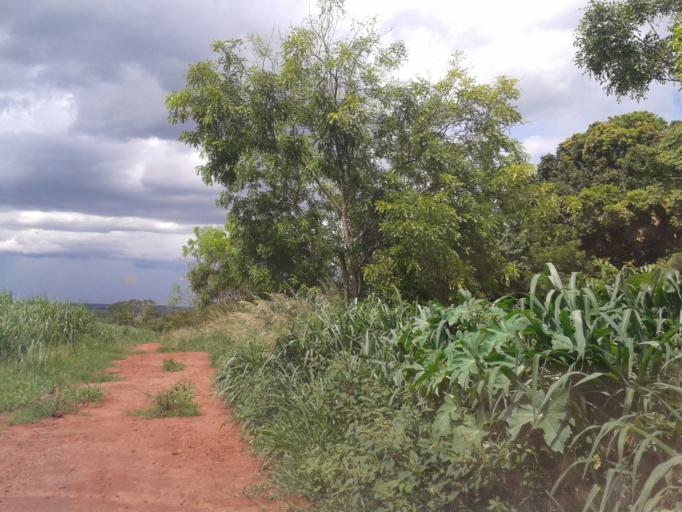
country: BR
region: Minas Gerais
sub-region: Santa Vitoria
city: Santa Vitoria
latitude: -19.1553
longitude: -50.5946
